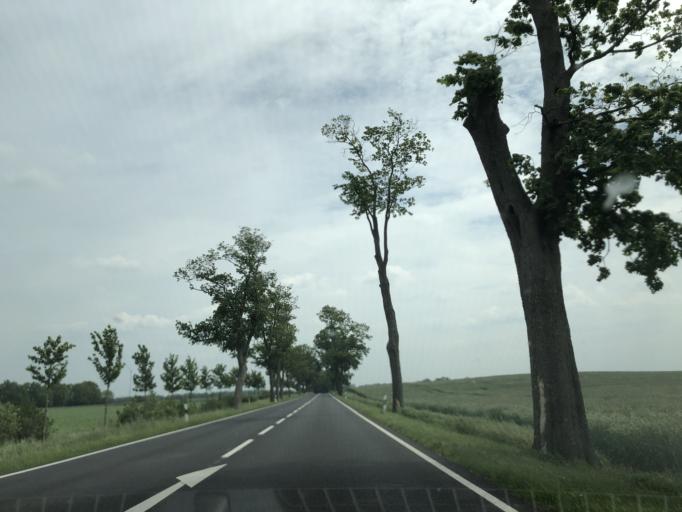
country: DE
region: Brandenburg
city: Gumtow
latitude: 52.9768
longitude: 12.2617
